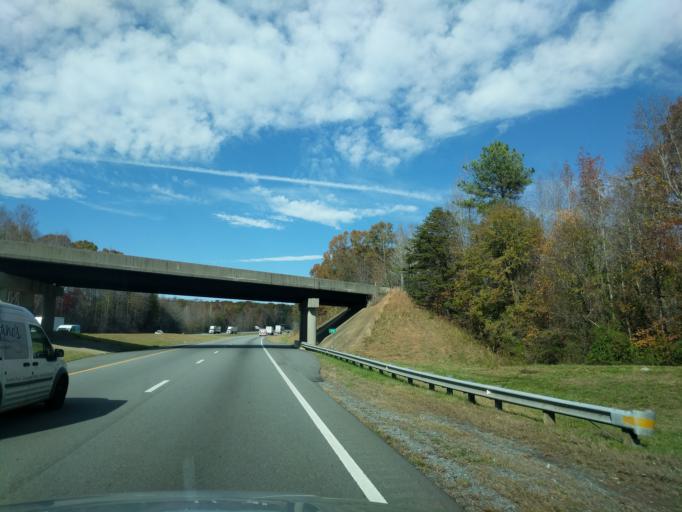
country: US
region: North Carolina
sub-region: Gaston County
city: Dallas
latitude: 35.3888
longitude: -81.2060
